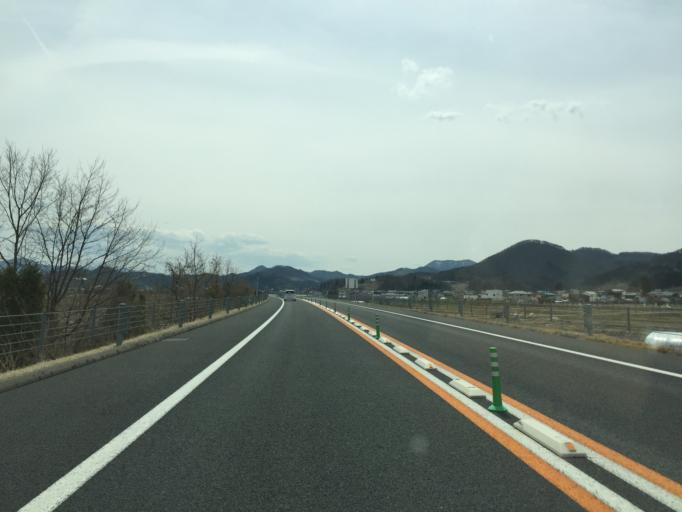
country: JP
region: Yamagata
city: Kaminoyama
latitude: 38.2389
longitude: 140.2753
